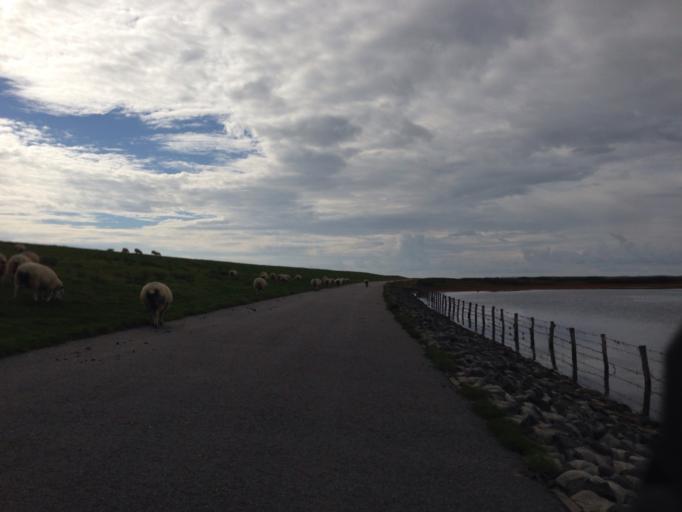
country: DE
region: Schleswig-Holstein
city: Oldsum
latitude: 54.7475
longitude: 8.4483
